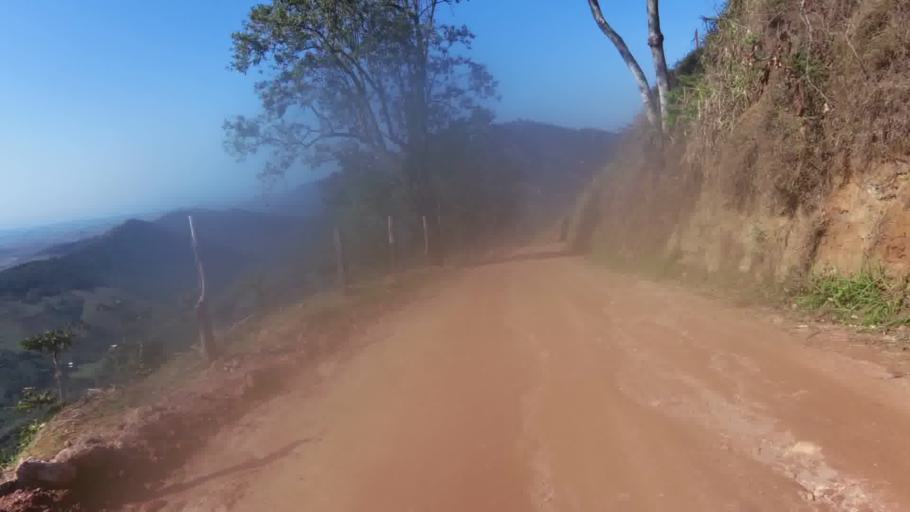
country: BR
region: Espirito Santo
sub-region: Alfredo Chaves
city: Alfredo Chaves
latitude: -20.6796
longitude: -40.7820
